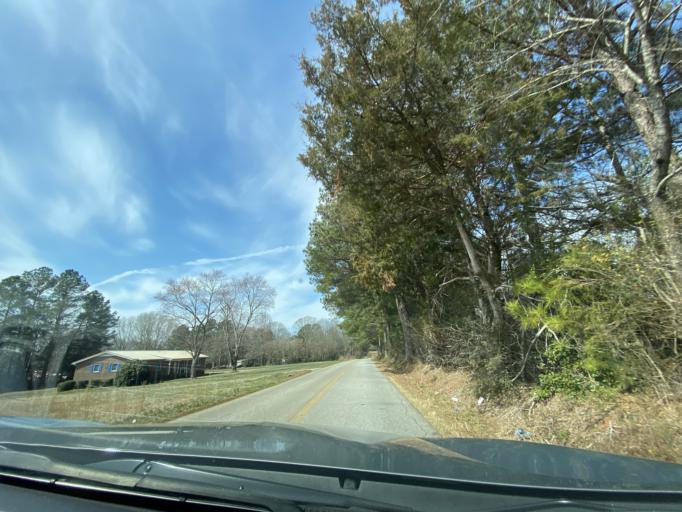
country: US
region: South Carolina
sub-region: Pickens County
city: Liberty
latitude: 34.8316
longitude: -82.7088
